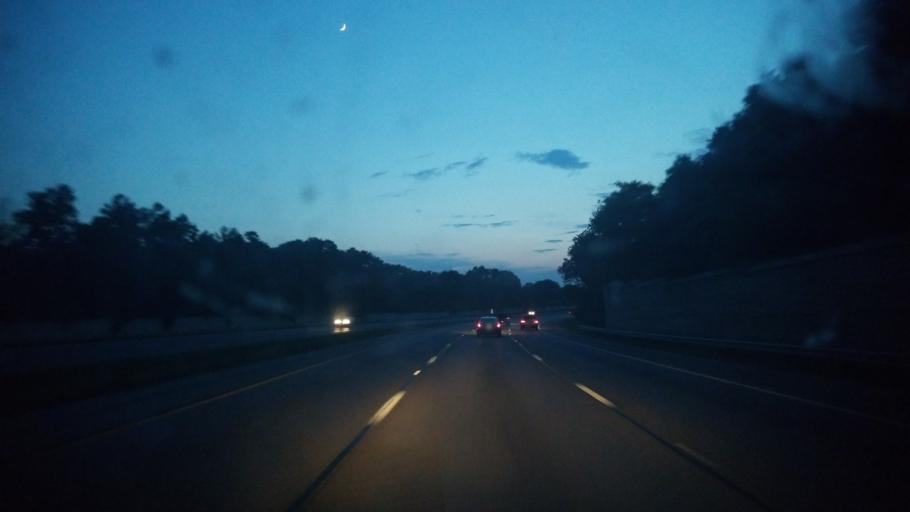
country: US
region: Ohio
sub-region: Hamilton County
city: Sixteen Mile Stand
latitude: 39.2528
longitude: -84.3237
